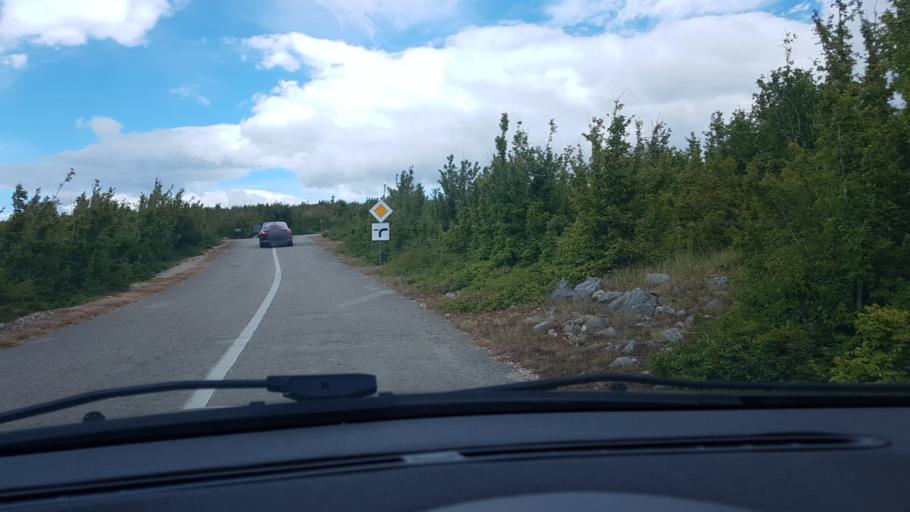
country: HR
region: Zadarska
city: Gracac
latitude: 44.1841
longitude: 15.8889
